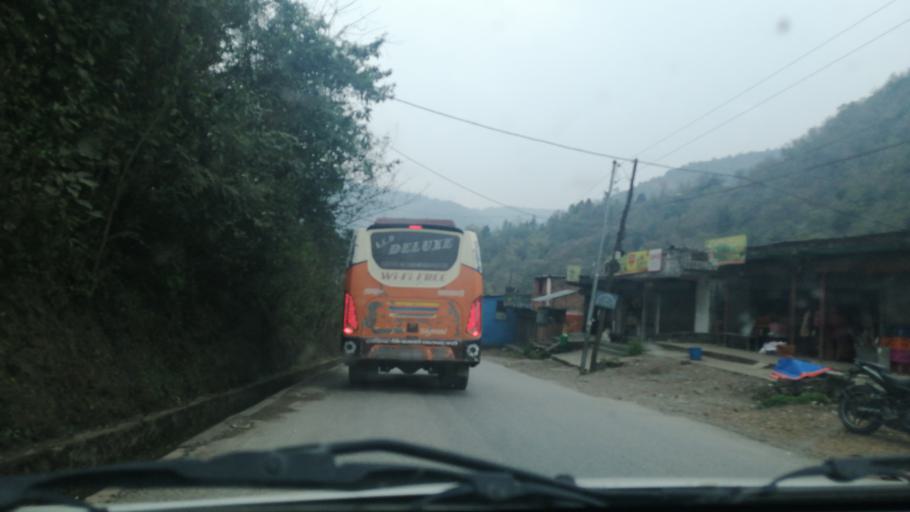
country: NP
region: Western Region
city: Tansen
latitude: 27.8120
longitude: 83.5235
